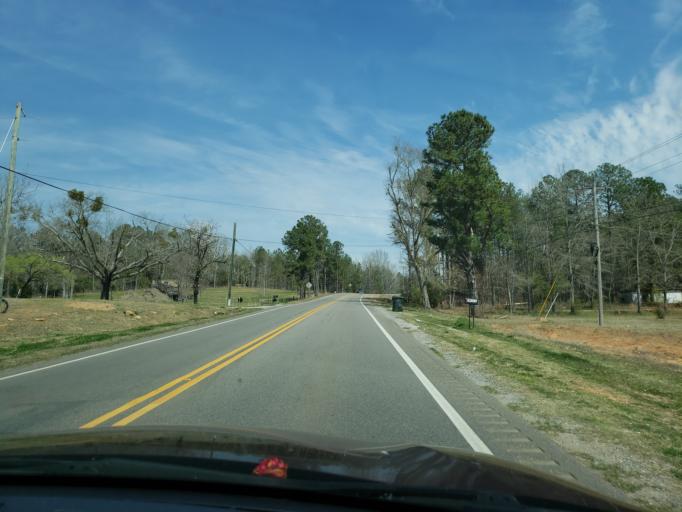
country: US
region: Alabama
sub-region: Elmore County
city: Wetumpka
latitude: 32.5671
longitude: -86.1246
